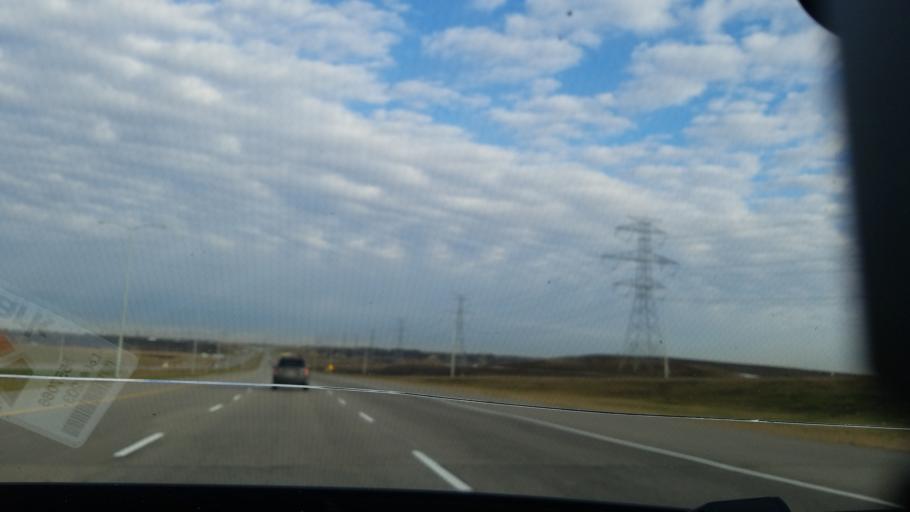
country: CA
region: Alberta
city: Sherwood Park
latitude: 53.5886
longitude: -113.3454
